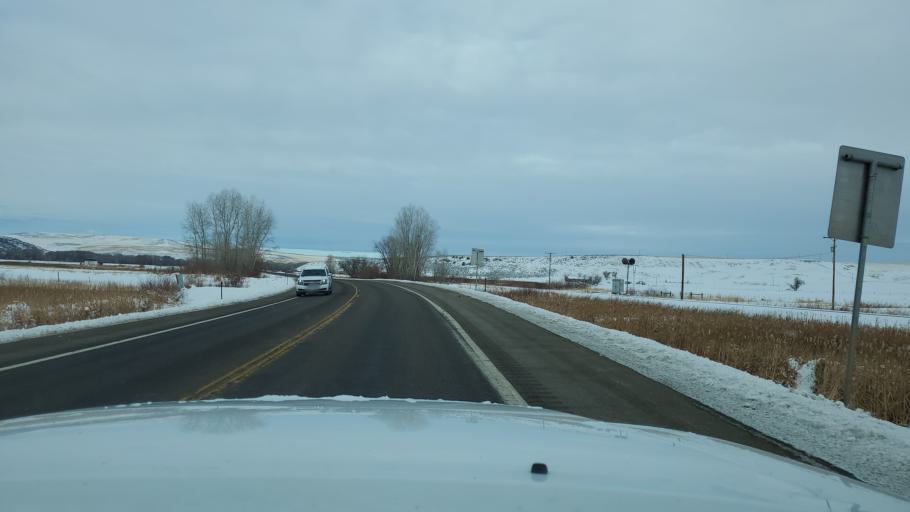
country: US
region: Colorado
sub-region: Routt County
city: Hayden
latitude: 40.4925
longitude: -107.3494
